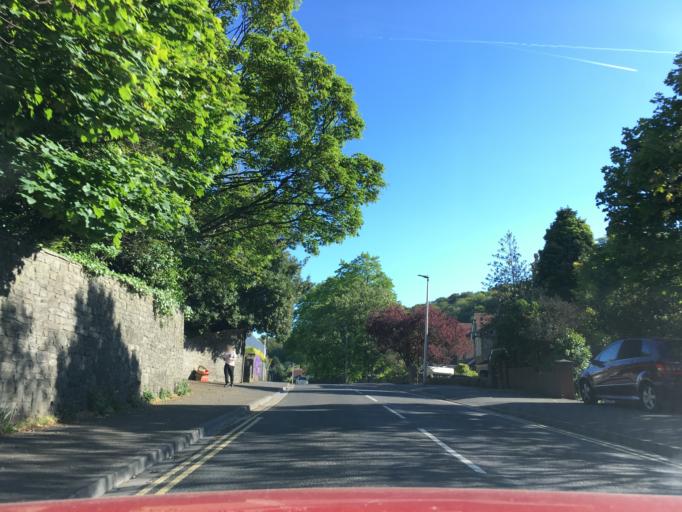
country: GB
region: England
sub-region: North Somerset
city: Clevedon
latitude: 51.4402
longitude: -2.8419
